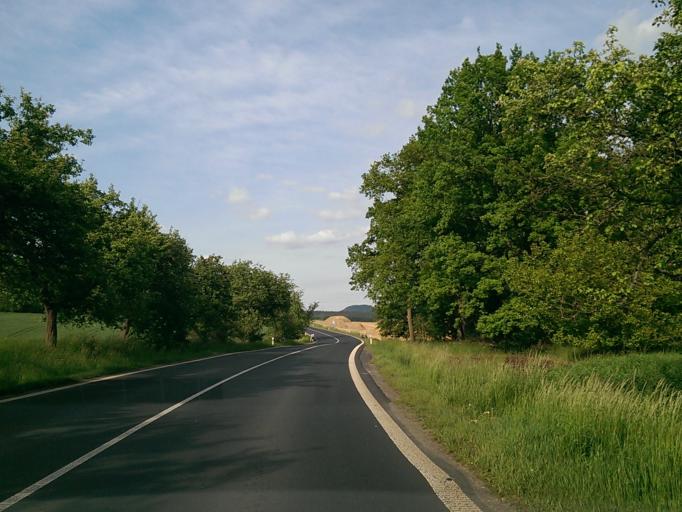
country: CZ
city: Duba
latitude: 50.5327
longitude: 14.5219
